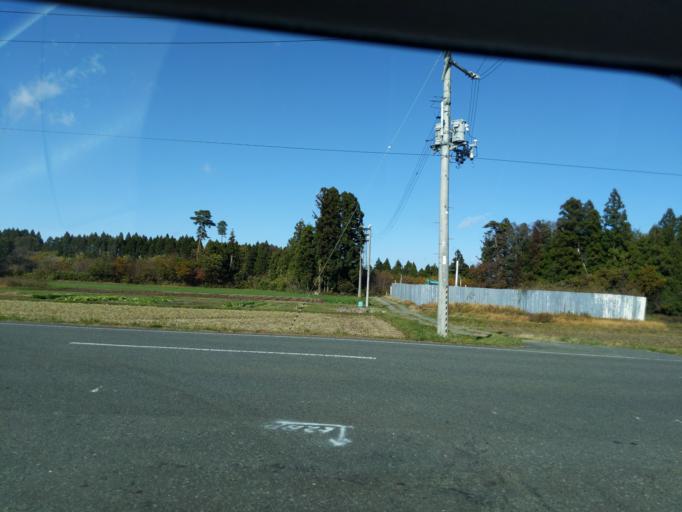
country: JP
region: Iwate
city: Mizusawa
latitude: 39.0951
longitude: 141.1225
